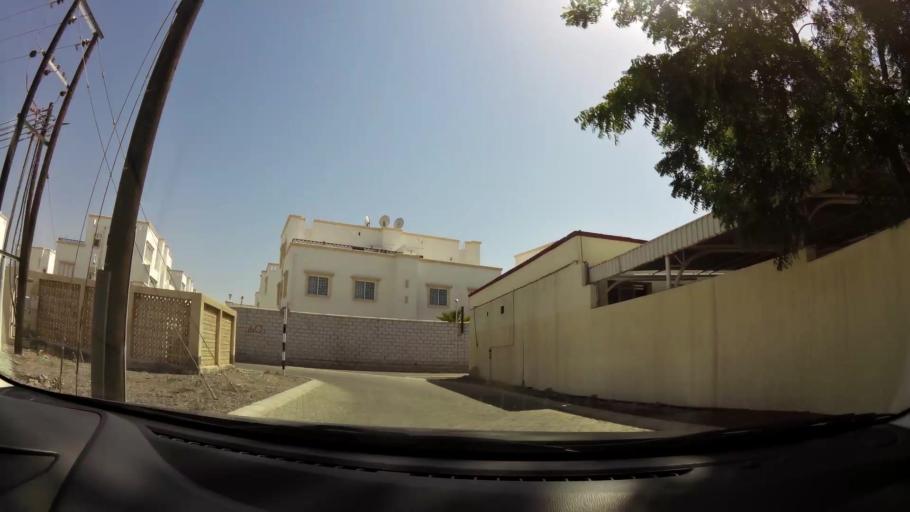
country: OM
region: Muhafazat Masqat
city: As Sib al Jadidah
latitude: 23.6395
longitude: 58.2220
